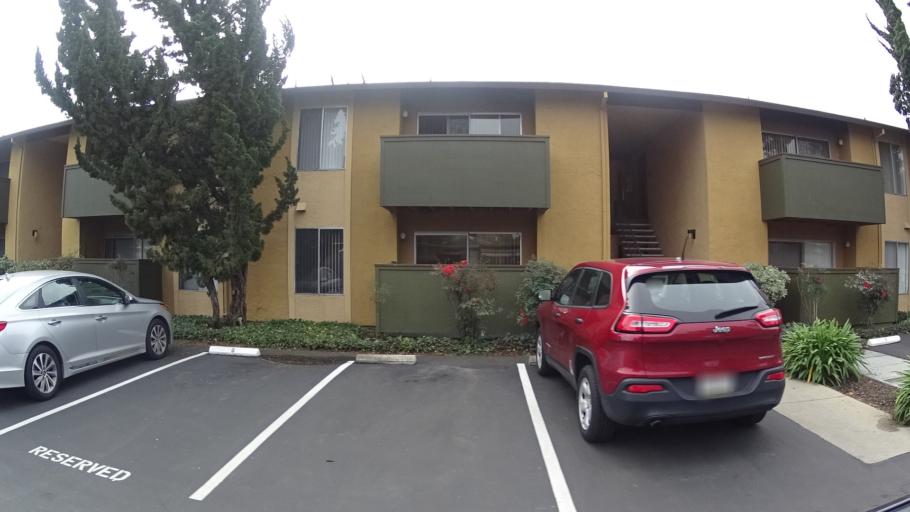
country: US
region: California
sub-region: Santa Clara County
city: Sunnyvale
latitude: 37.3584
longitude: -122.0151
